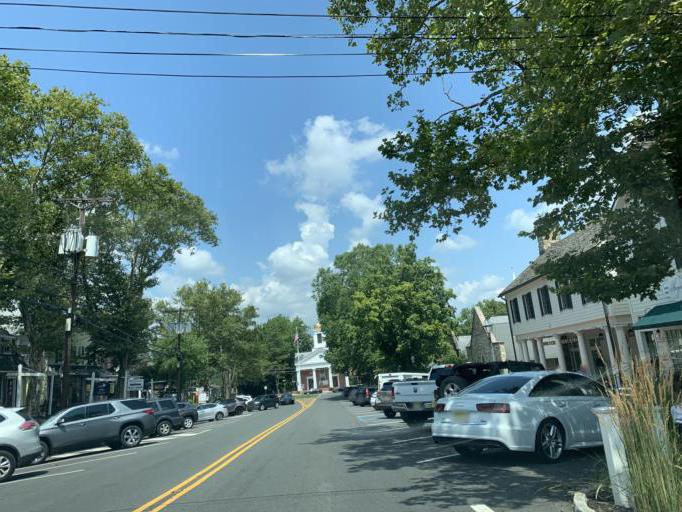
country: US
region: New Jersey
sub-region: Somerset County
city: Bernardsville
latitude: 40.7053
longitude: -74.5490
